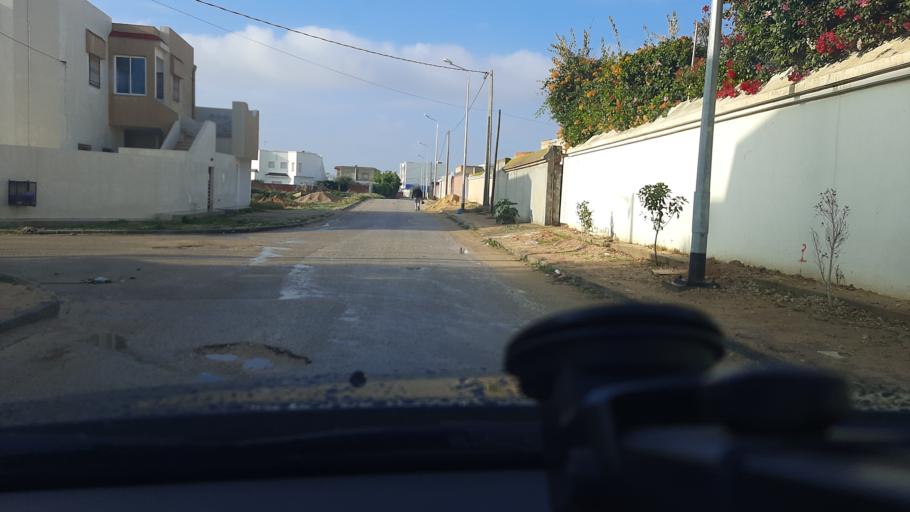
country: TN
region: Safaqis
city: Sfax
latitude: 34.7419
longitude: 10.7145
